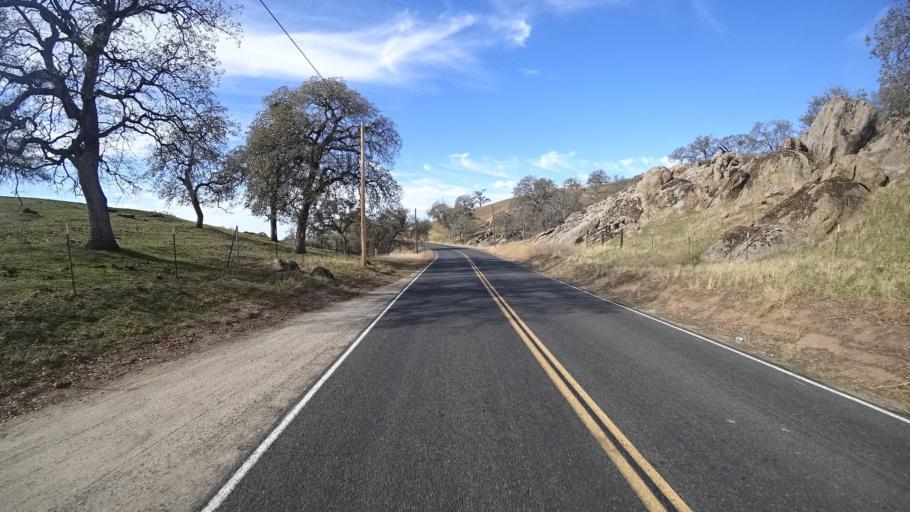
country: US
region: California
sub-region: Kern County
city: Alta Sierra
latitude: 35.6269
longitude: -118.8065
